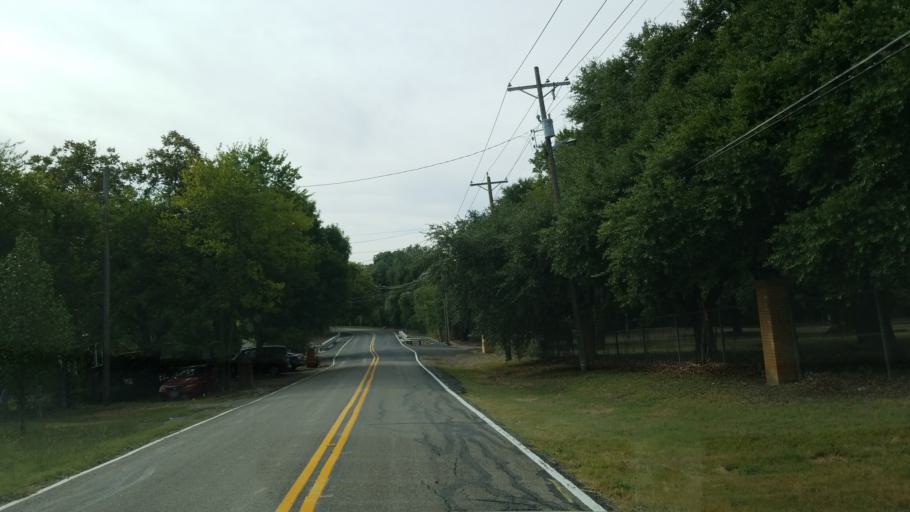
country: US
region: Texas
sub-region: Dallas County
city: Dallas
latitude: 32.7768
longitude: -96.7210
